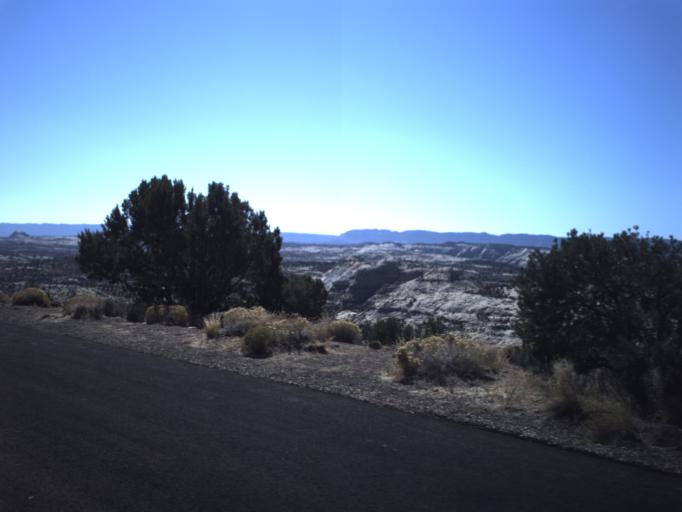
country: US
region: Utah
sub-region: Wayne County
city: Loa
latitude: 37.8397
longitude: -111.4215
